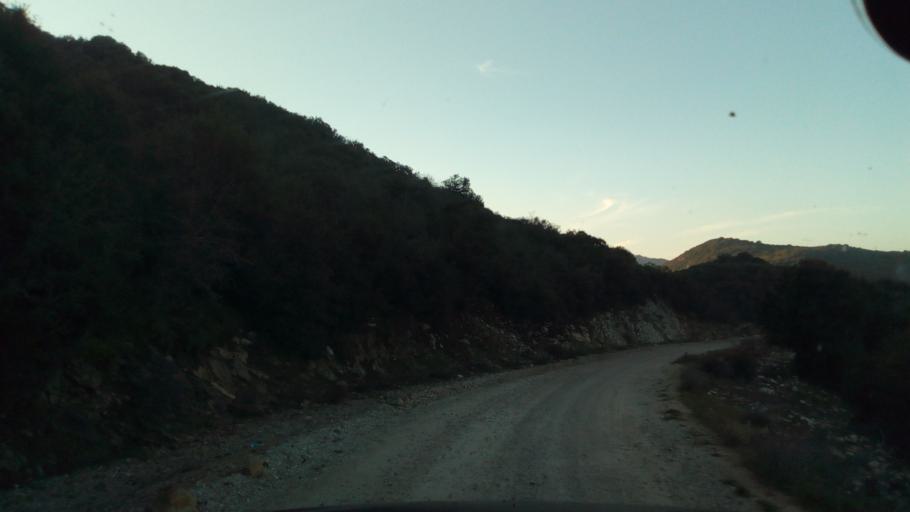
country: GR
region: West Greece
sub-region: Nomos Aitolias kai Akarnanias
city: Nafpaktos
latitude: 38.4656
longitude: 21.8263
